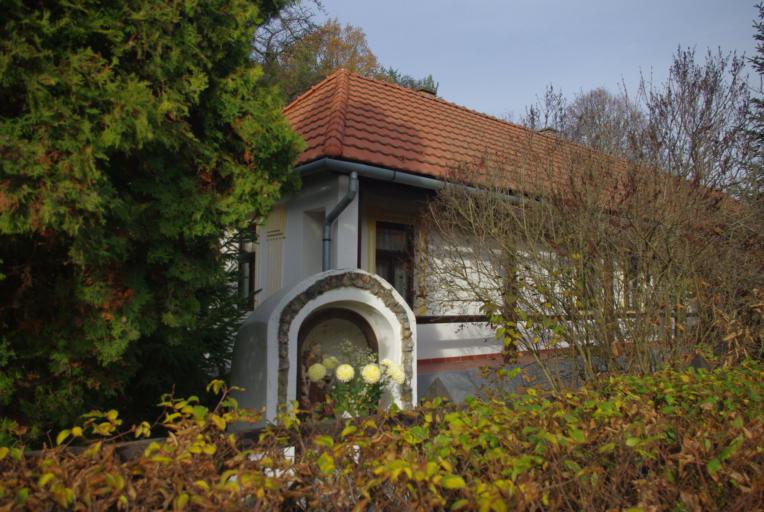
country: HU
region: Borsod-Abauj-Zemplen
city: Sarospatak
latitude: 48.4486
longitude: 21.4794
